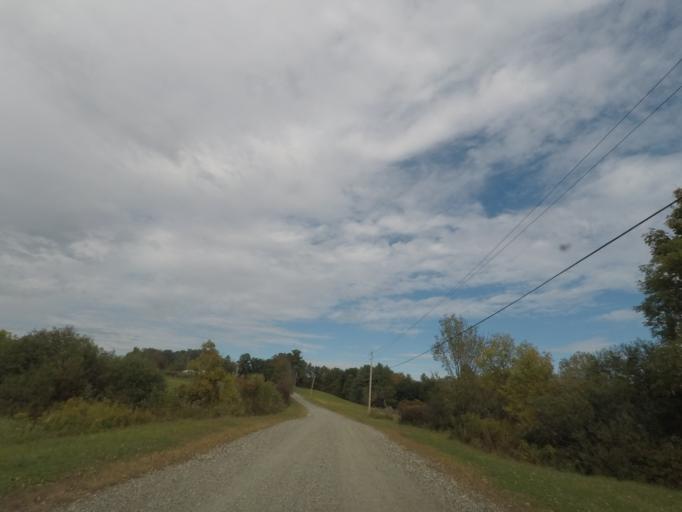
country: US
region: New York
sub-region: Rensselaer County
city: Nassau
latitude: 42.5751
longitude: -73.6161
